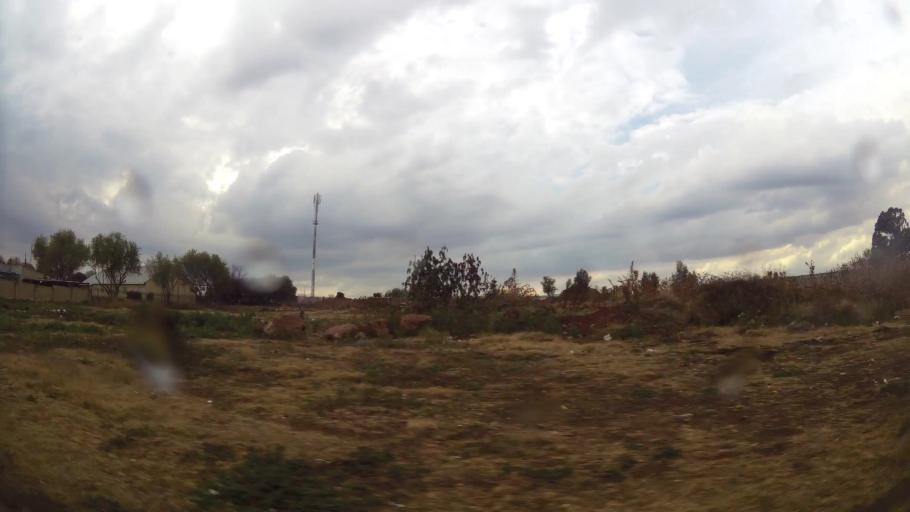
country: ZA
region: Gauteng
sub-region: Ekurhuleni Metropolitan Municipality
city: Germiston
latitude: -26.3814
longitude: 28.1299
